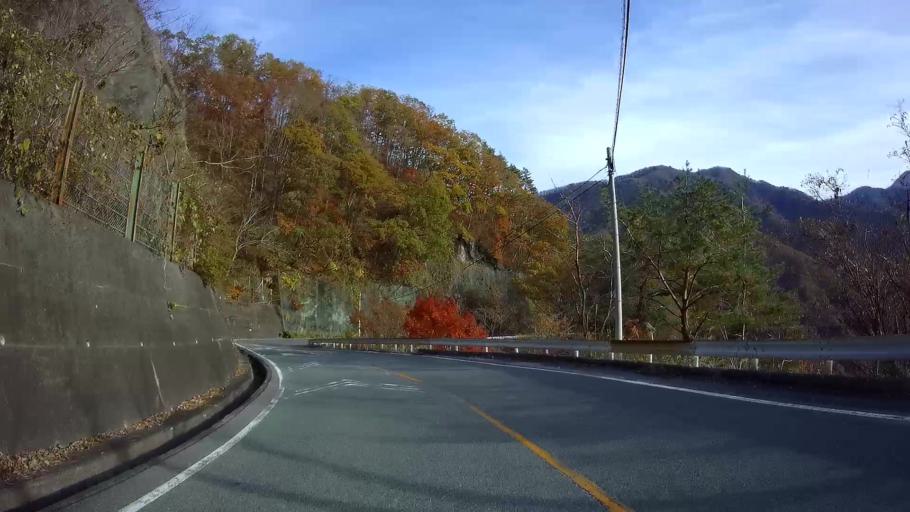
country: JP
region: Yamanashi
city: Fujikawaguchiko
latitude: 35.4790
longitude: 138.5514
